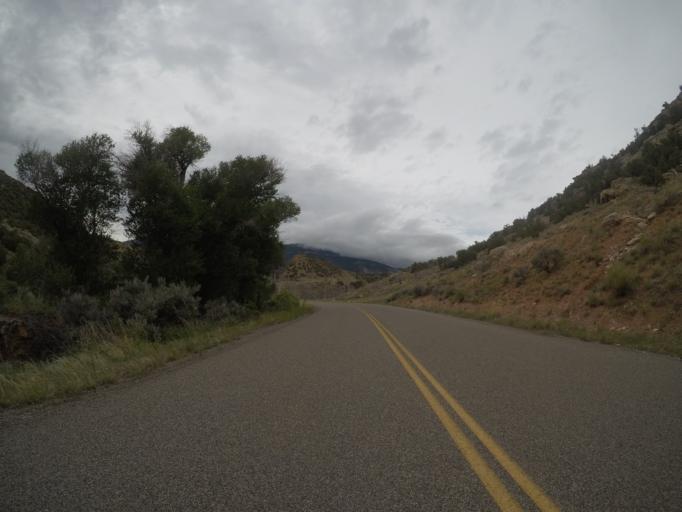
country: US
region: Wyoming
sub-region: Big Horn County
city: Lovell
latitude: 45.1072
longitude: -108.2275
